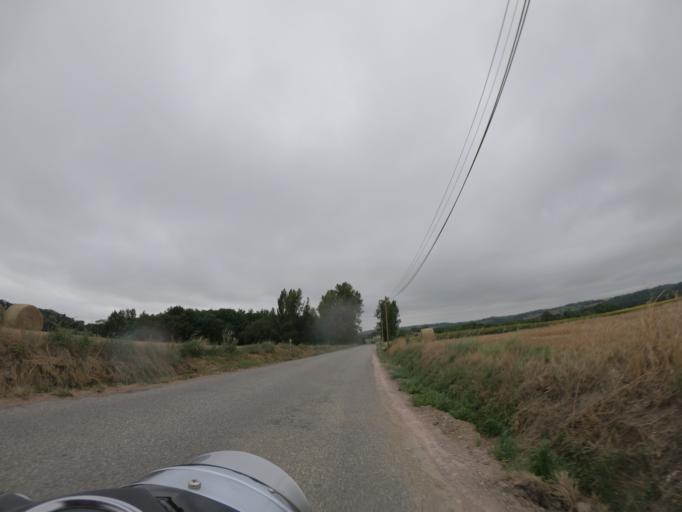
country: FR
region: Midi-Pyrenees
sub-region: Departement de l'Ariege
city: La Tour-du-Crieu
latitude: 43.1002
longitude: 1.7211
